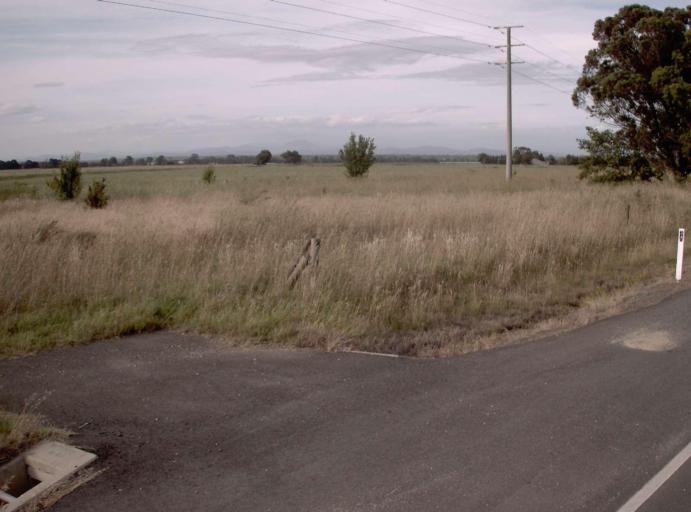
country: AU
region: Victoria
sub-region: Wellington
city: Heyfield
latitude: -38.0215
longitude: 146.7657
